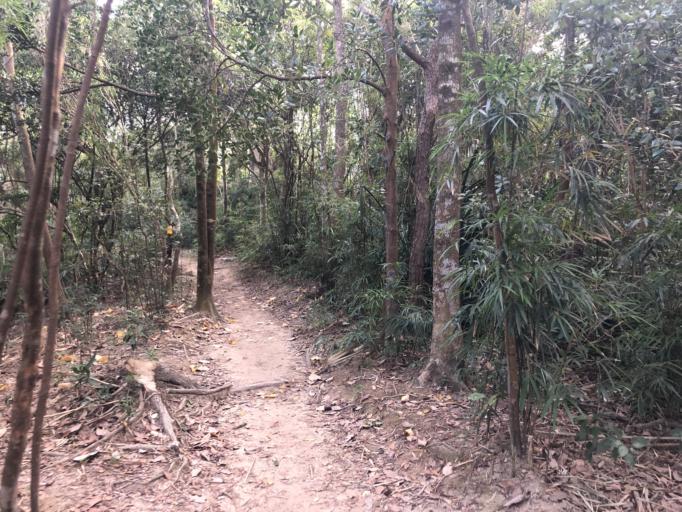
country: HK
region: Wanchai
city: Wan Chai
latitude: 22.2764
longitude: 114.2112
